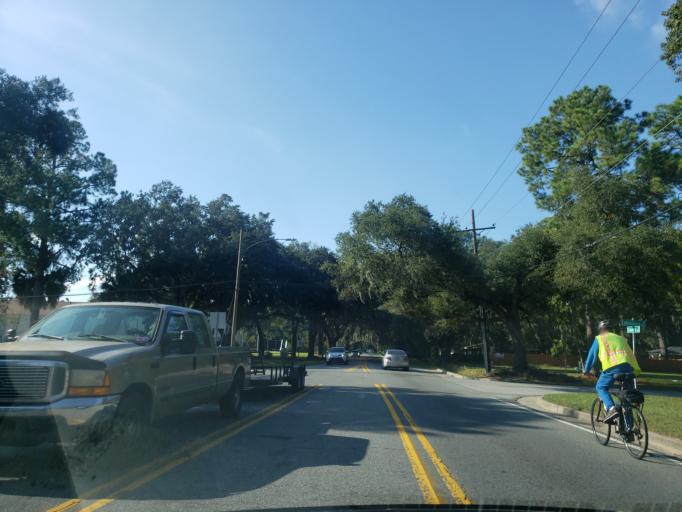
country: US
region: Georgia
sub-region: Chatham County
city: Thunderbolt
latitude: 32.0186
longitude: -81.0755
